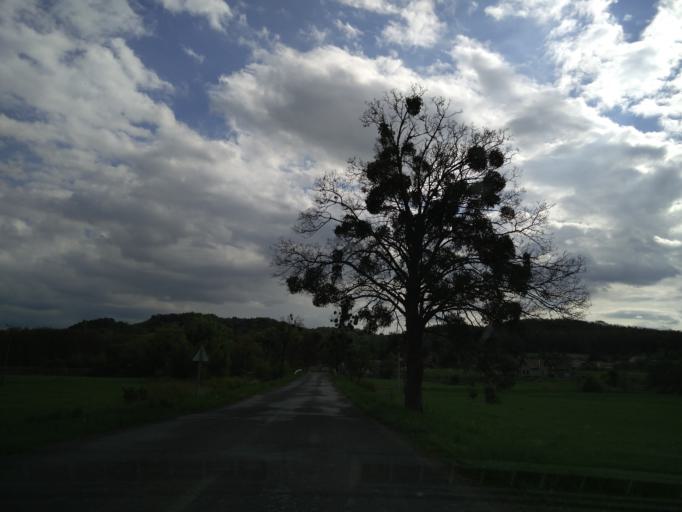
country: HU
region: Zala
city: Zalaegerszeg
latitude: 46.8813
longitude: 16.9222
